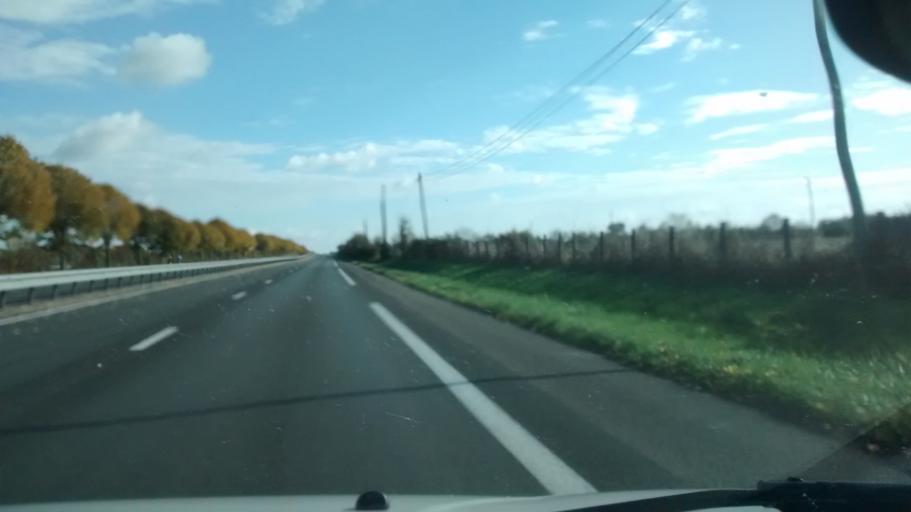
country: FR
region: Pays de la Loire
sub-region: Departement de Maine-et-Loire
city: Pouance
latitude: 47.7340
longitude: -1.1341
